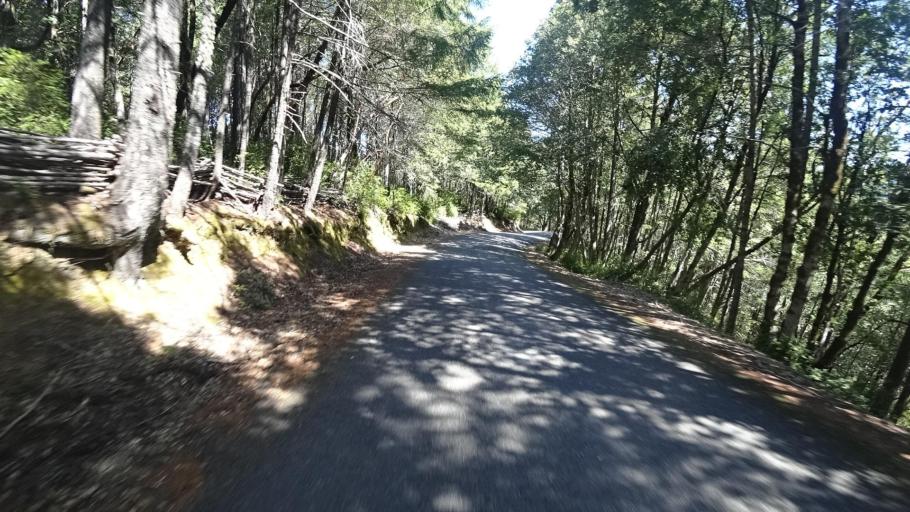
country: US
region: California
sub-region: Humboldt County
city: Rio Dell
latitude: 40.2112
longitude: -124.1049
